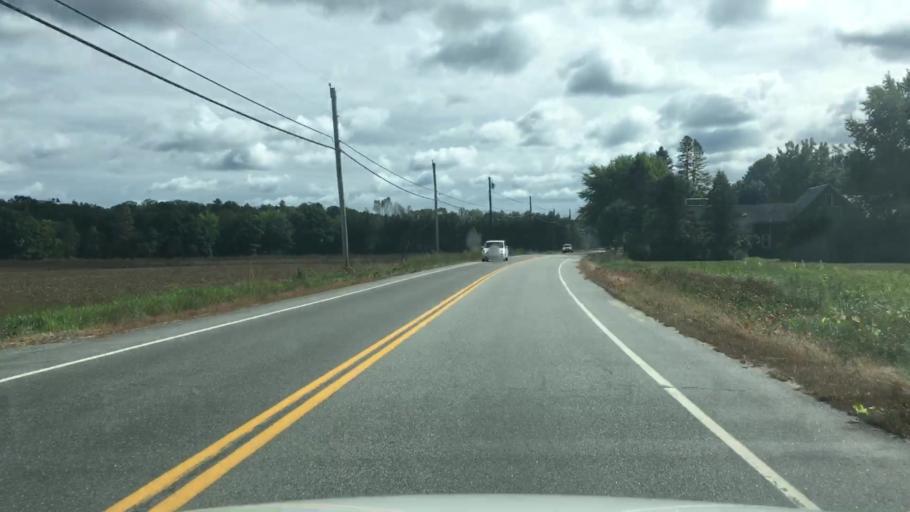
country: US
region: Maine
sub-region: Androscoggin County
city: Lisbon
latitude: 44.0171
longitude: -70.1709
